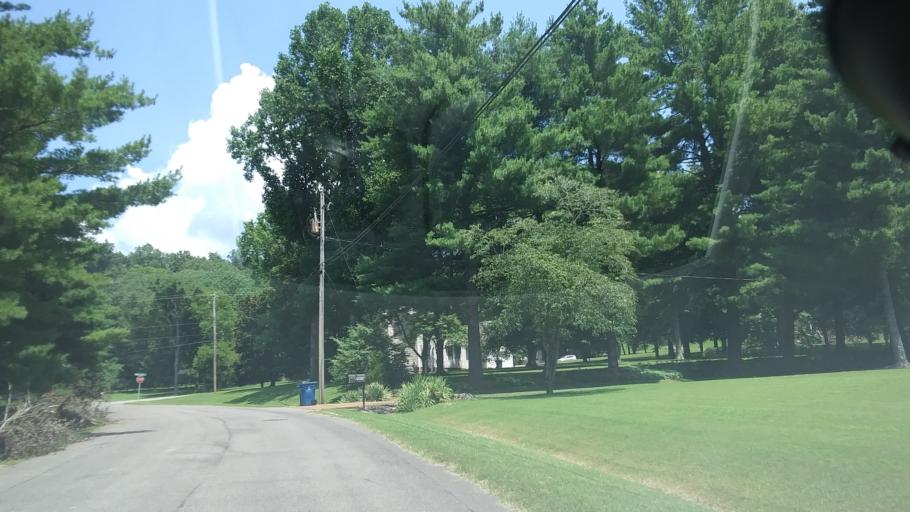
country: US
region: Tennessee
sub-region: Davidson County
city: Belle Meade
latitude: 36.0886
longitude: -86.9479
